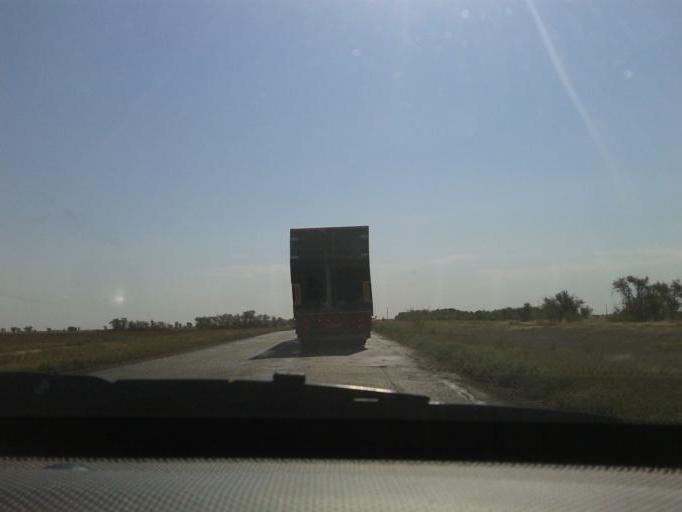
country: RU
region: Astrakhan
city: Znamensk
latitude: 48.6221
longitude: 45.5371
